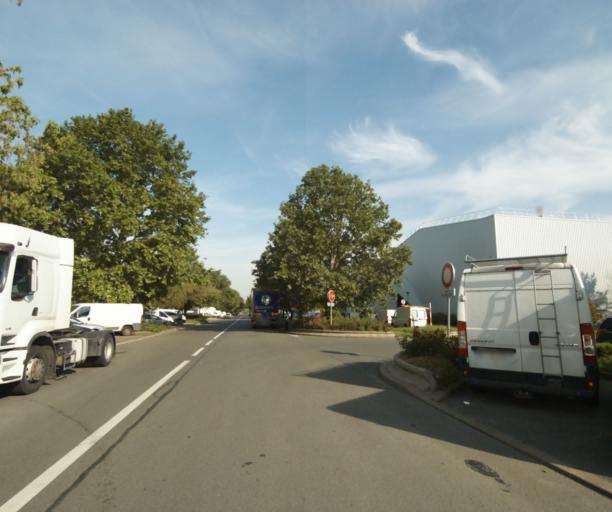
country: FR
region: Ile-de-France
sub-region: Departement des Hauts-de-Seine
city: Bois-Colombes
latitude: 48.9403
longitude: 2.2793
